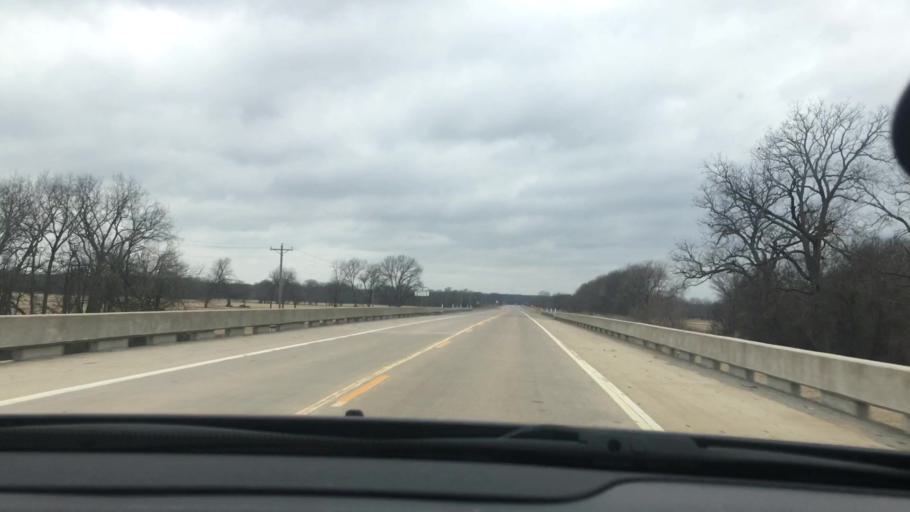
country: US
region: Oklahoma
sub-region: Atoka County
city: Atoka
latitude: 34.3719
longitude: -96.3130
